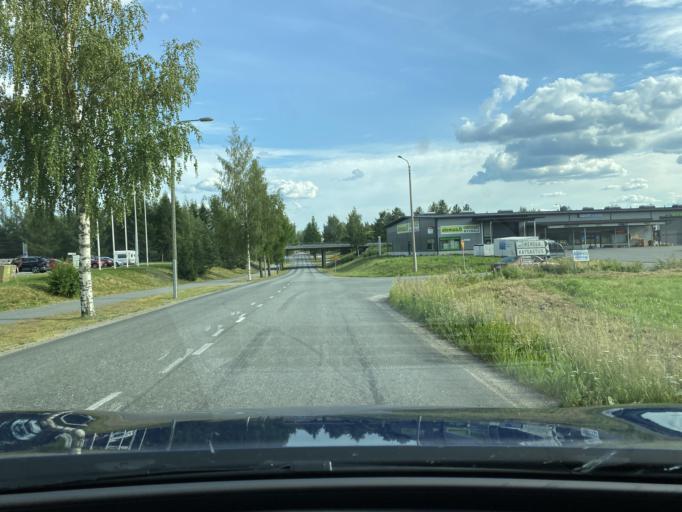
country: FI
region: Southern Ostrobothnia
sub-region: Kuusiokunnat
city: Alavus
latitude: 62.5938
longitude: 23.6081
